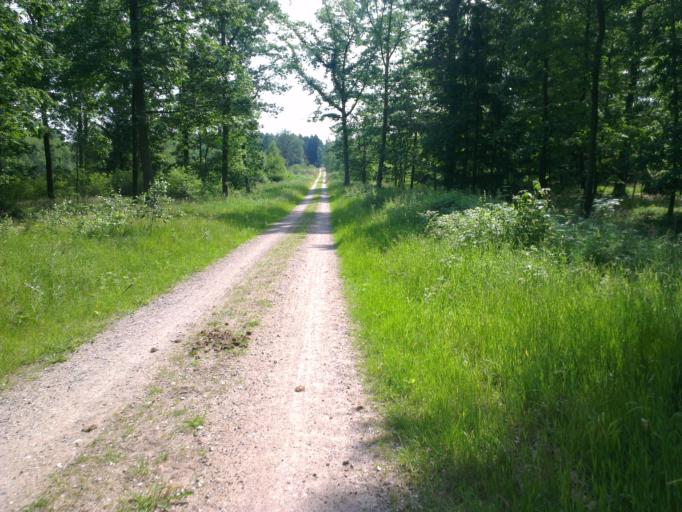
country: DK
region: Capital Region
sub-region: Allerod Kommune
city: Lillerod
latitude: 55.9125
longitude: 12.3613
